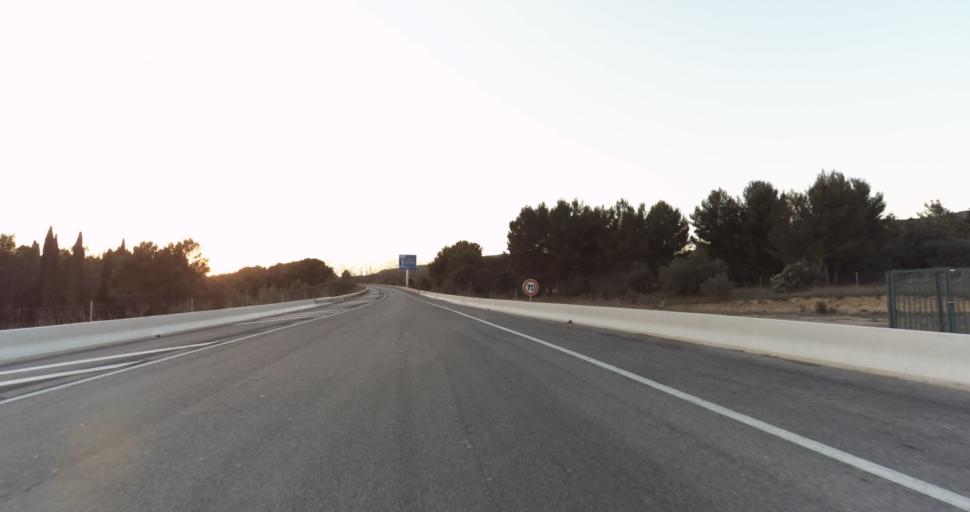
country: FR
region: Provence-Alpes-Cote d'Azur
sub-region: Departement des Bouches-du-Rhone
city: Coudoux
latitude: 43.5532
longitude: 5.2380
